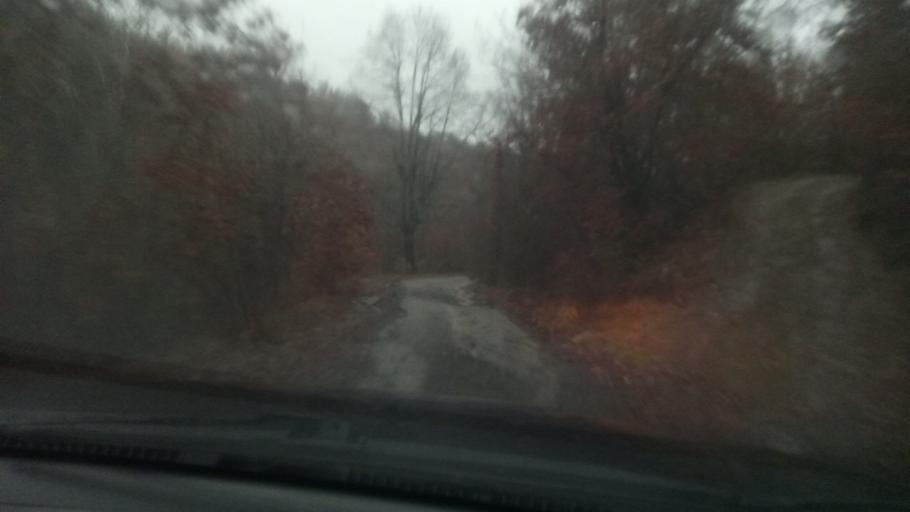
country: MK
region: Vinica
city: Blatec
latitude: 41.8385
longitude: 22.6110
